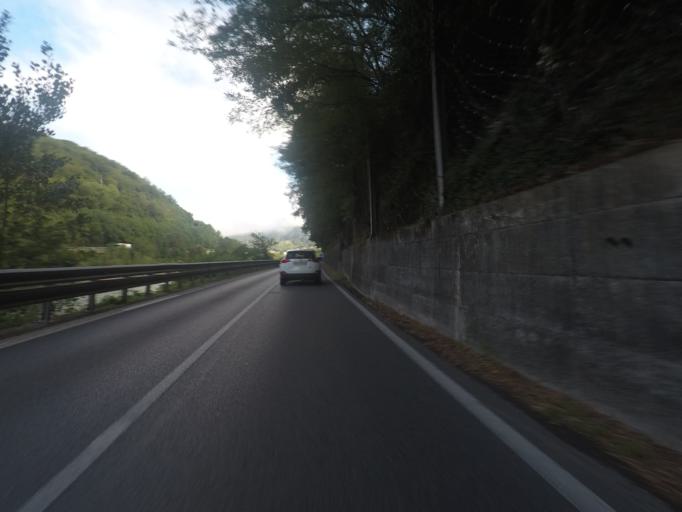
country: IT
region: Tuscany
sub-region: Provincia di Lucca
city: Bagni di Lucca
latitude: 43.9914
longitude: 10.5533
